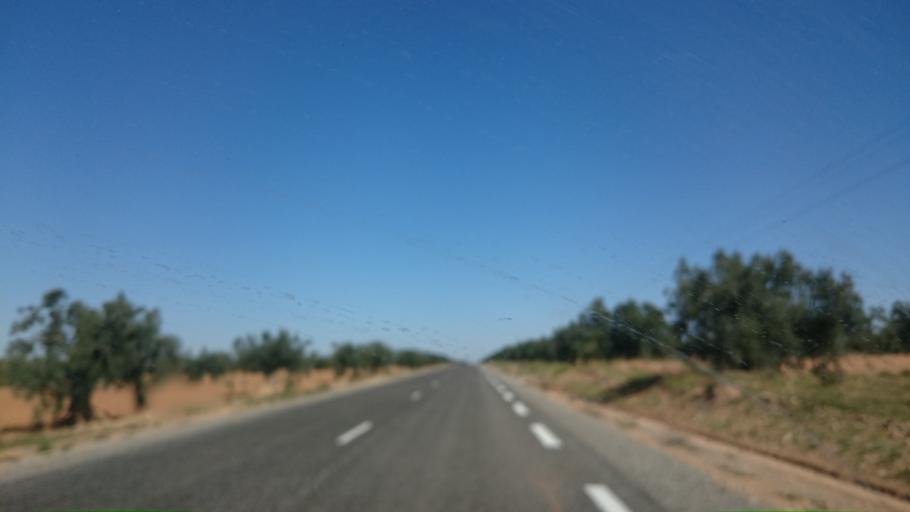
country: TN
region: Safaqis
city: Sfax
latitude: 34.8414
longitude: 10.4562
